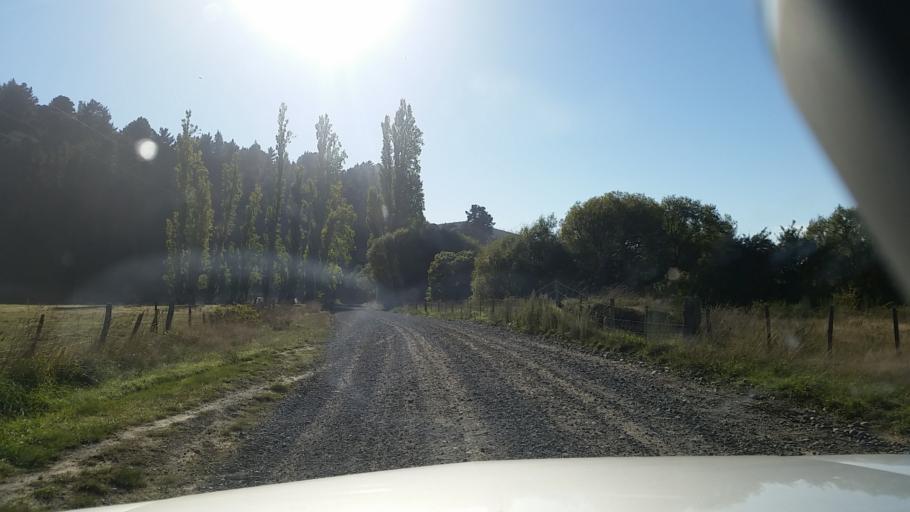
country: NZ
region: Marlborough
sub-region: Marlborough District
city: Blenheim
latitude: -41.4482
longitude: 173.8774
